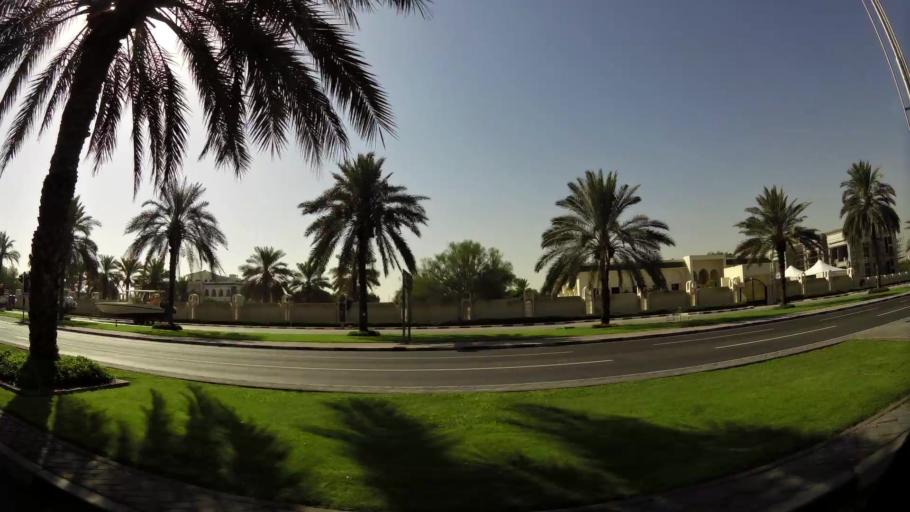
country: AE
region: Dubai
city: Dubai
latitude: 25.1298
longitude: 55.1857
